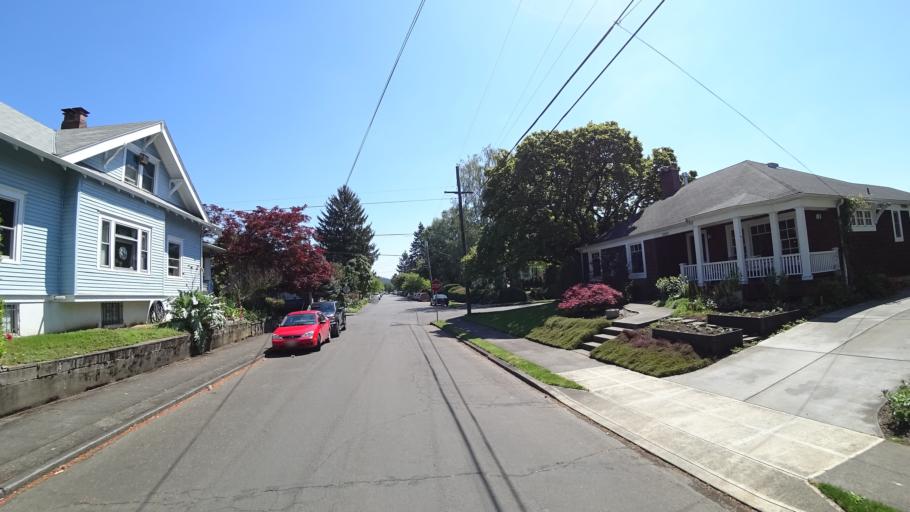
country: US
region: Oregon
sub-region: Multnomah County
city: Portland
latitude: 45.5088
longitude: -122.6300
